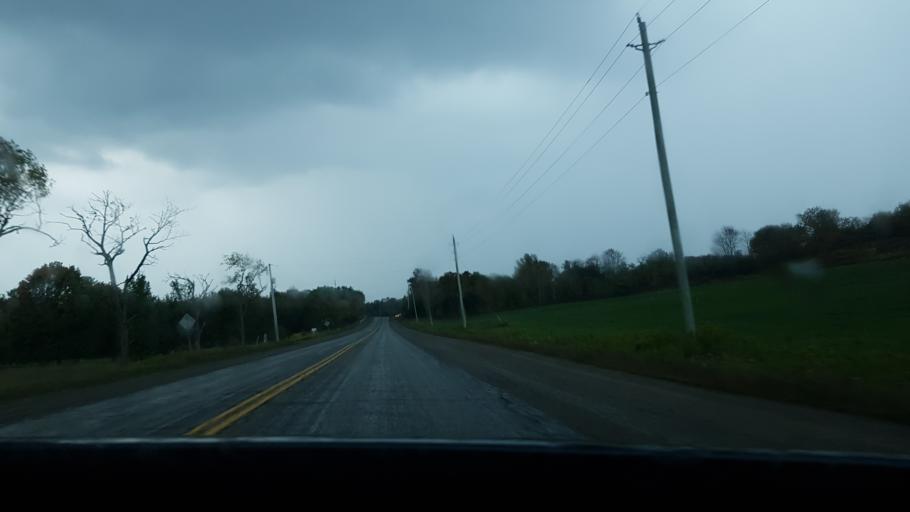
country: CA
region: Ontario
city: Omemee
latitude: 44.3564
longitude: -78.5406
